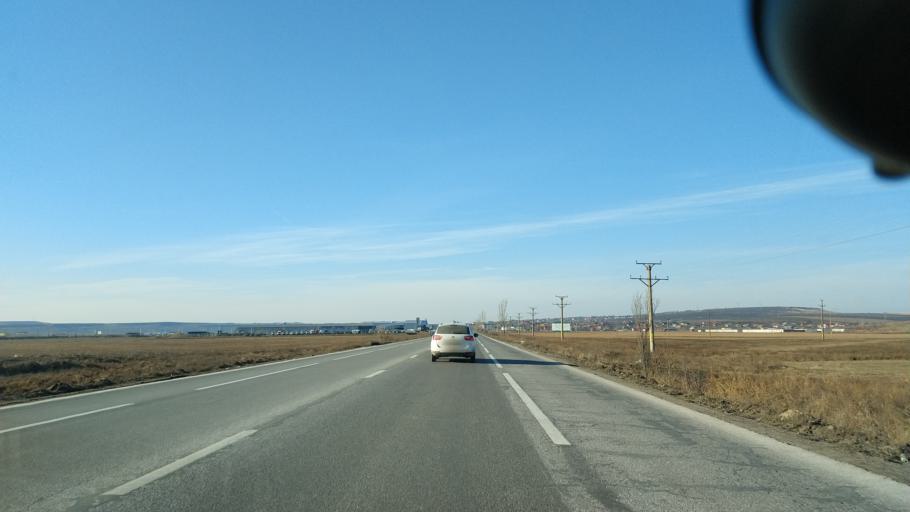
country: RO
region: Iasi
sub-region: Comuna Letcani
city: Letcani
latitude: 47.1872
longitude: 27.4435
